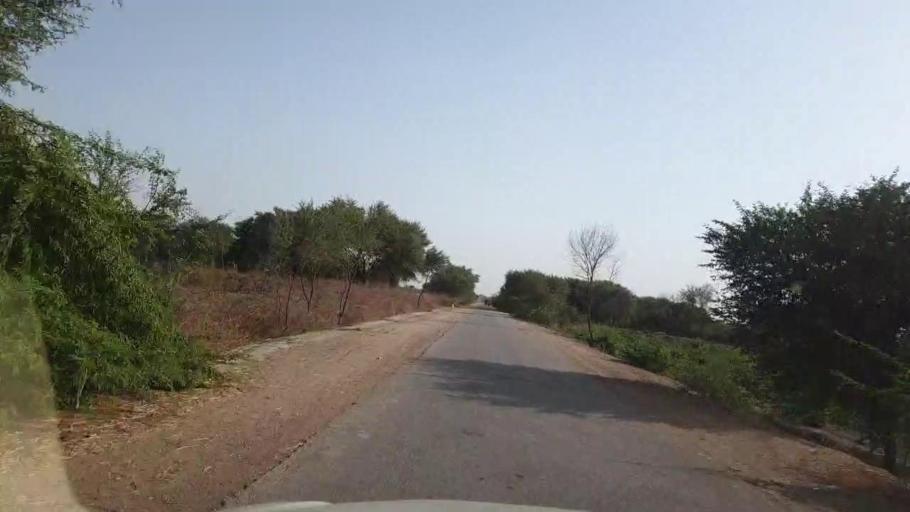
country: PK
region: Sindh
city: Tando Ghulam Ali
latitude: 25.0974
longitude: 68.8689
